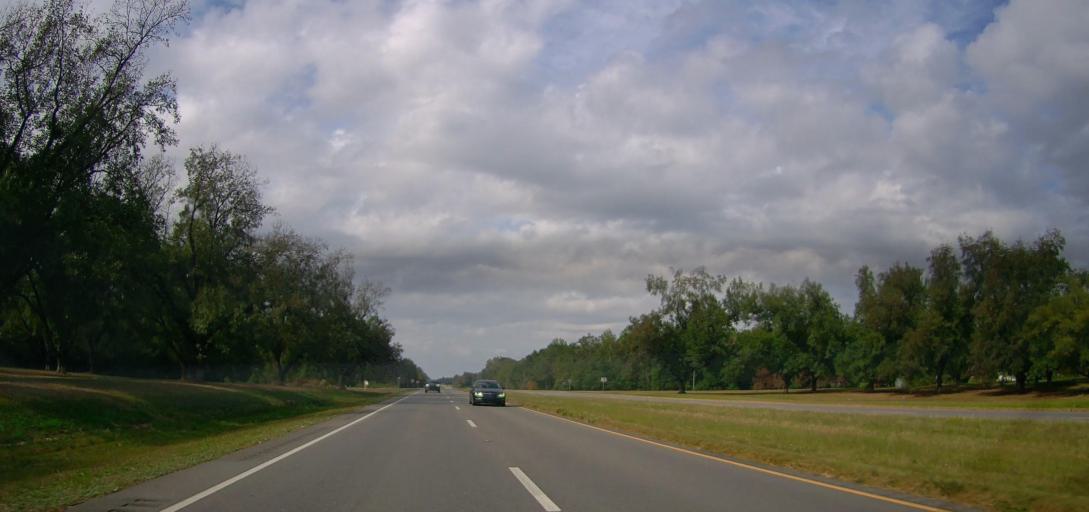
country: US
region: Georgia
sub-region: Thomas County
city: Meigs
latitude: 31.0121
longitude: -84.0537
